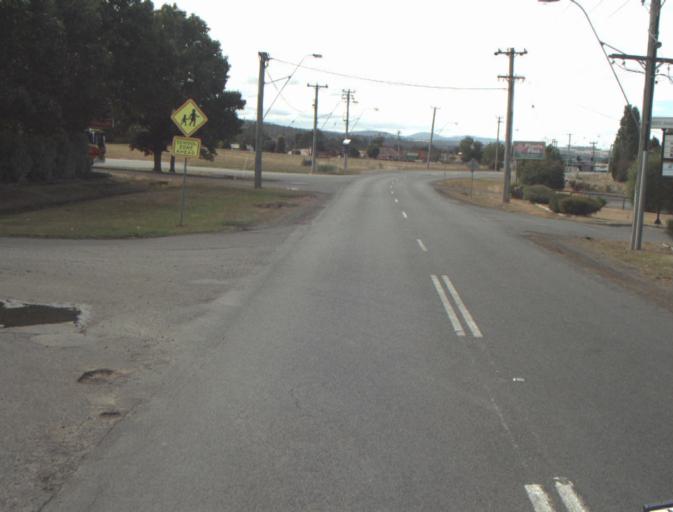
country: AU
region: Tasmania
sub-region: Launceston
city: Mayfield
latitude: -41.3767
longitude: 147.1245
